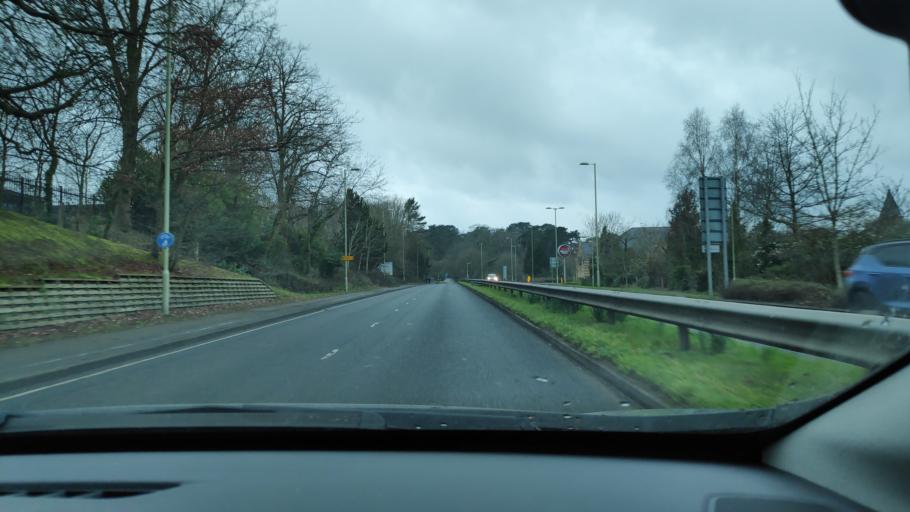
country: GB
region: England
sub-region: Hampshire
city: Aldershot
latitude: 51.2501
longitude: -0.7749
